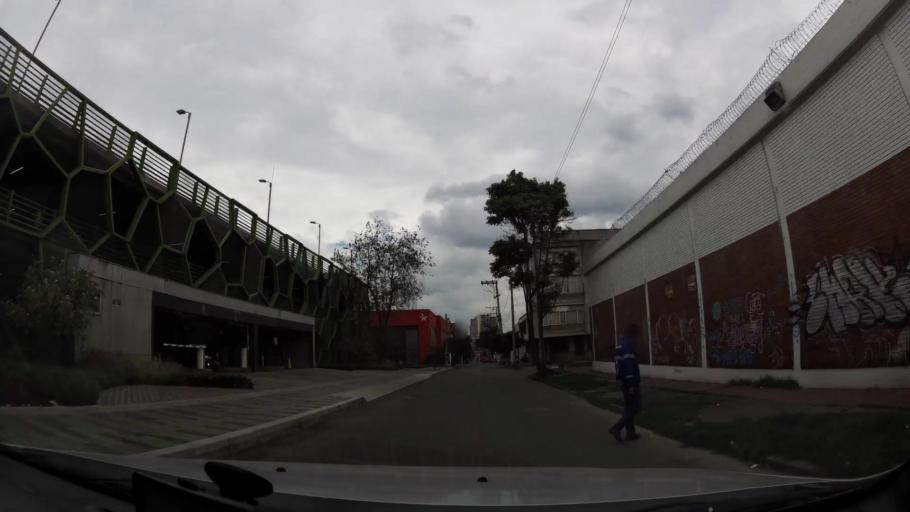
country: CO
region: Bogota D.C.
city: Bogota
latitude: 4.6284
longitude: -74.0861
